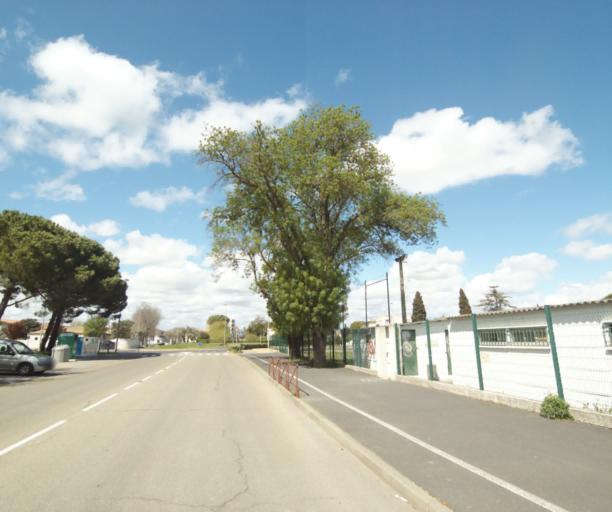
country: FR
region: Languedoc-Roussillon
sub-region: Departement de l'Herault
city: Lattes
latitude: 43.5675
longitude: 3.9071
